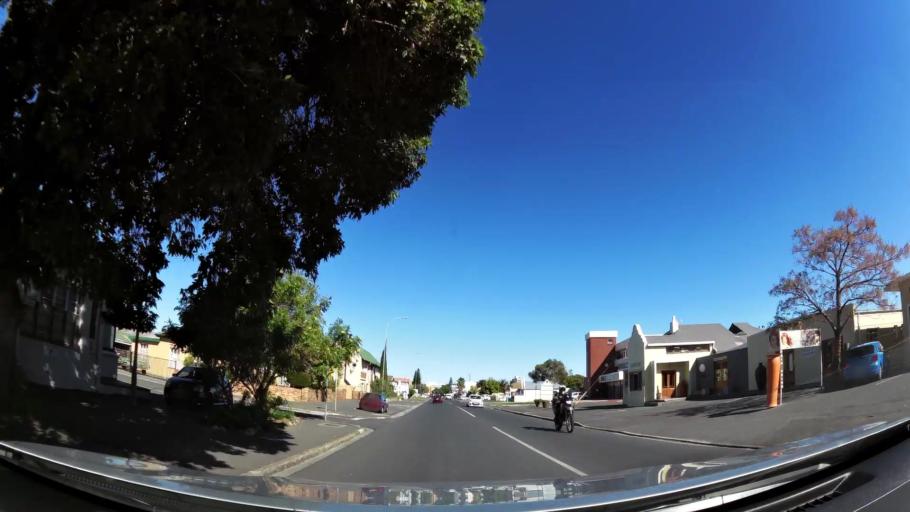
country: ZA
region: Western Cape
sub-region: Cape Winelands District Municipality
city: Stellenbosch
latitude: -34.1116
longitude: 18.8343
